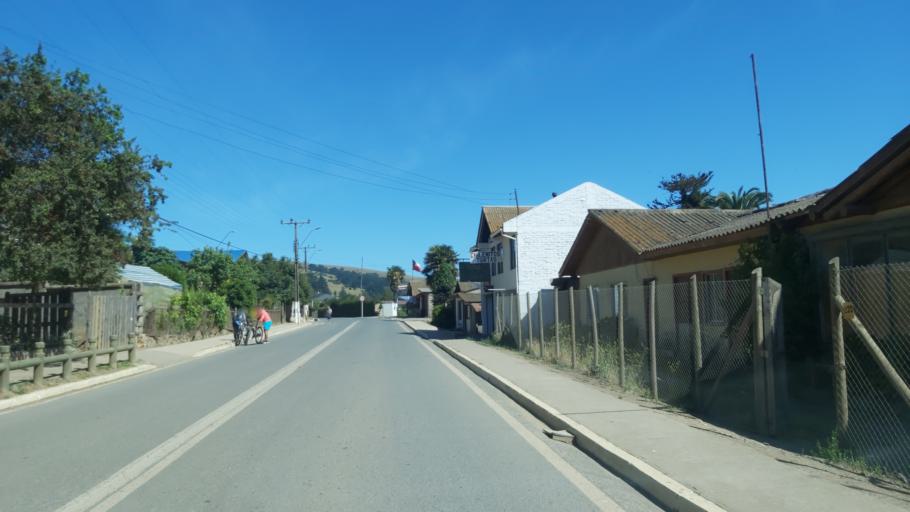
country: CL
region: Maule
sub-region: Provincia de Talca
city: Constitucion
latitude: -34.7666
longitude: -72.0741
